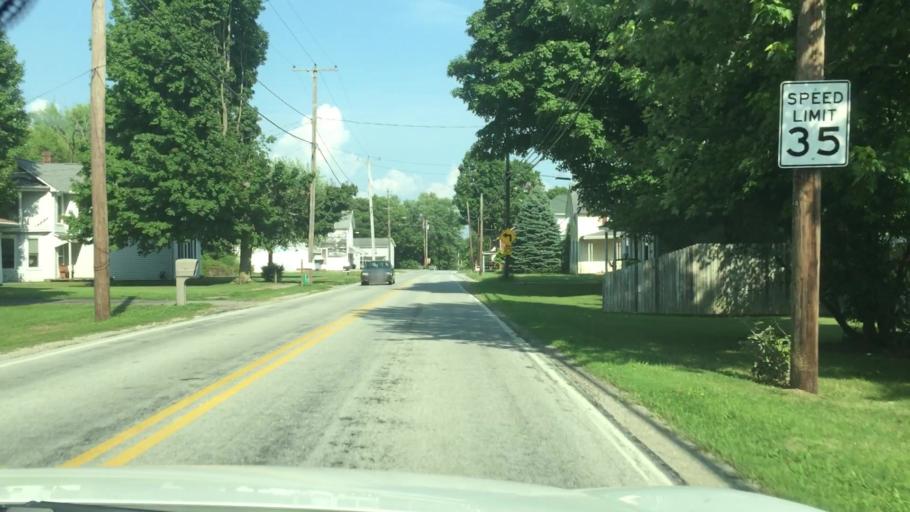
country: US
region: Ohio
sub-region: Clark County
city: Northridge
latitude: 39.9923
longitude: -83.7180
